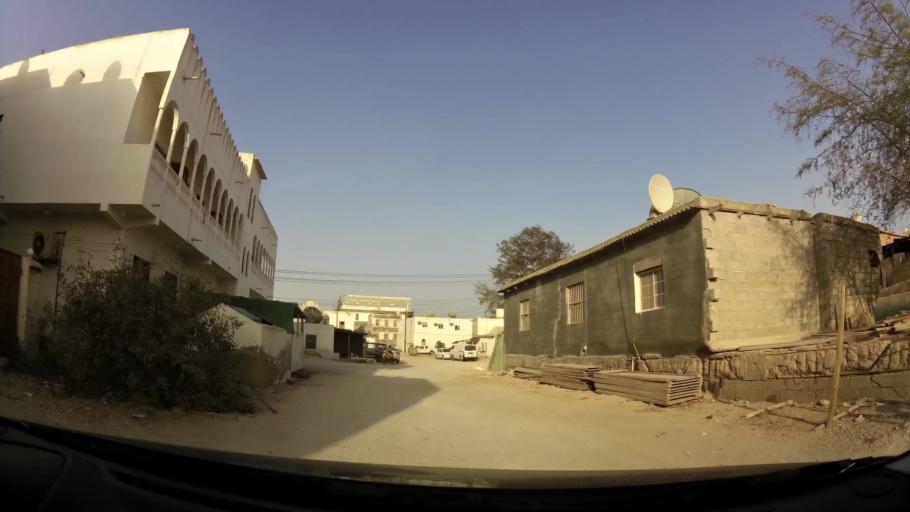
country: OM
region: Zufar
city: Salalah
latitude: 17.0095
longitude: 54.0881
